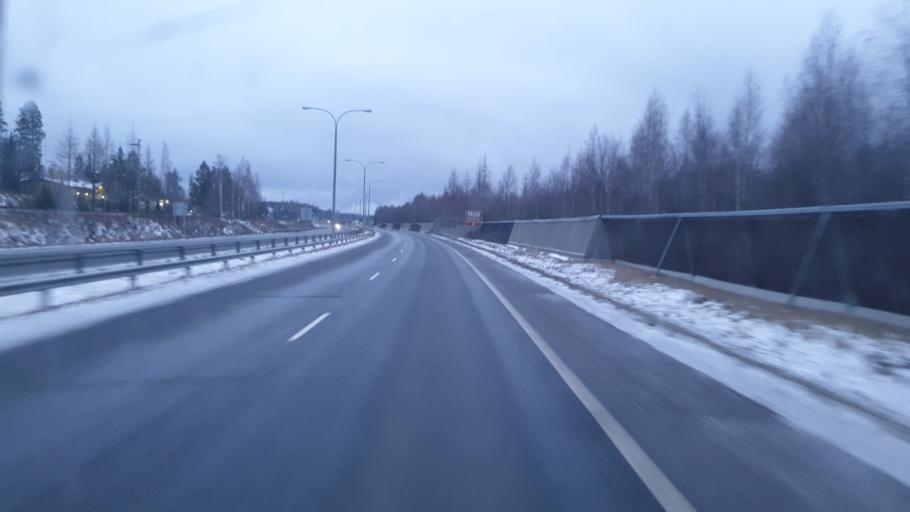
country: FI
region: Northern Savo
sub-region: Kuopio
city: Kuopio
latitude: 62.9819
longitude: 27.7062
